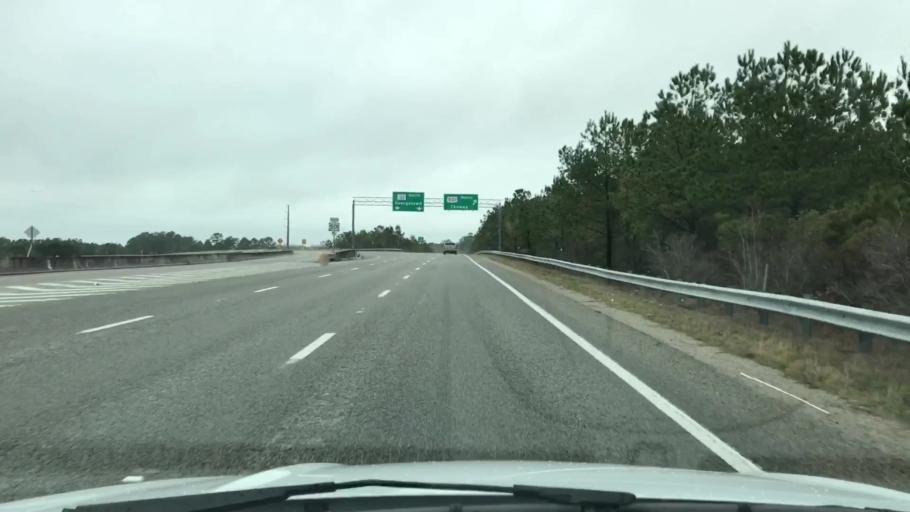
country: US
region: South Carolina
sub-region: Horry County
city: Forestbrook
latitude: 33.7415
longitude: -78.9488
